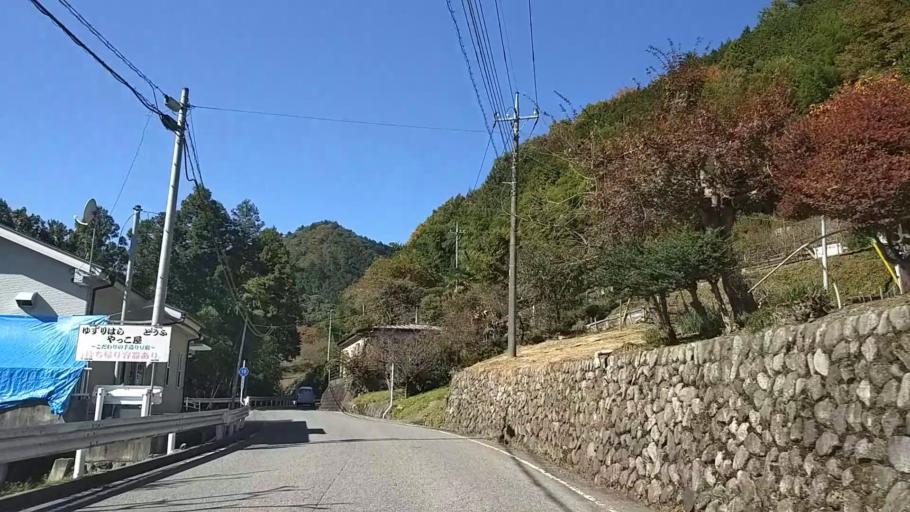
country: JP
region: Yamanashi
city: Uenohara
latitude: 35.6791
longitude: 139.0745
